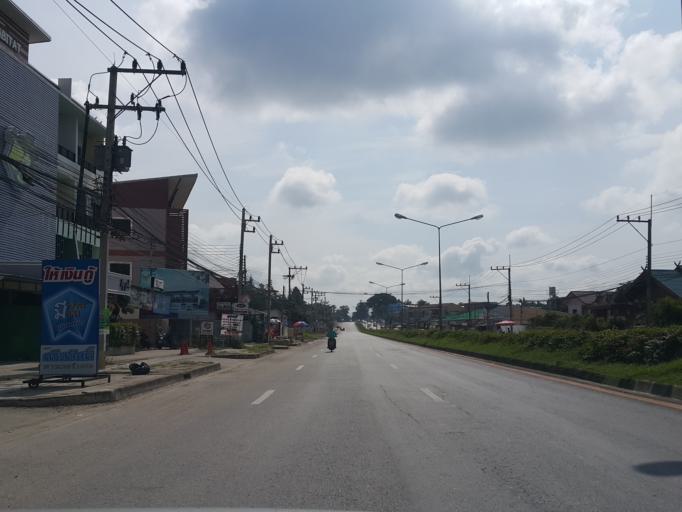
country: TH
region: Chiang Mai
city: San Sai
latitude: 18.8901
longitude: 99.0235
